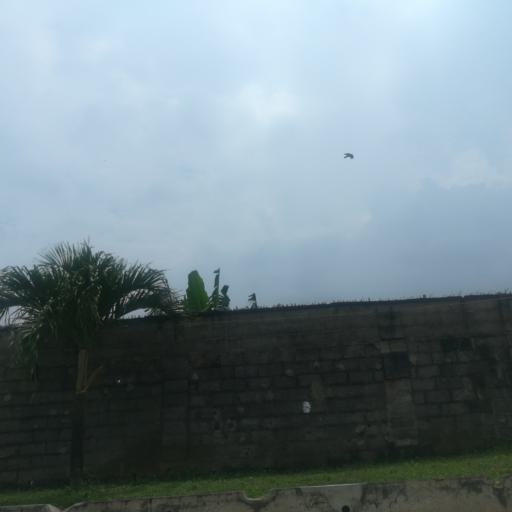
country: NG
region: Lagos
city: Ojota
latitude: 6.5786
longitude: 3.3857
